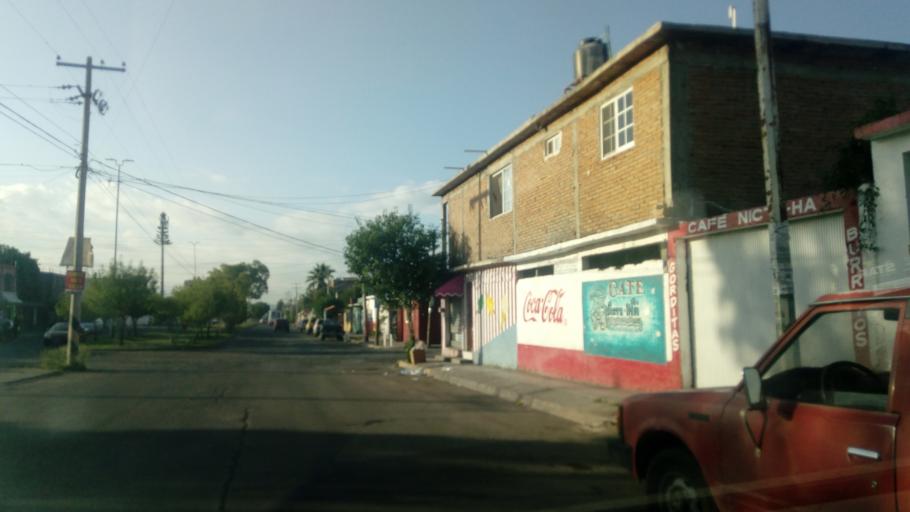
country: MX
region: Durango
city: Victoria de Durango
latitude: 24.0460
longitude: -104.6144
